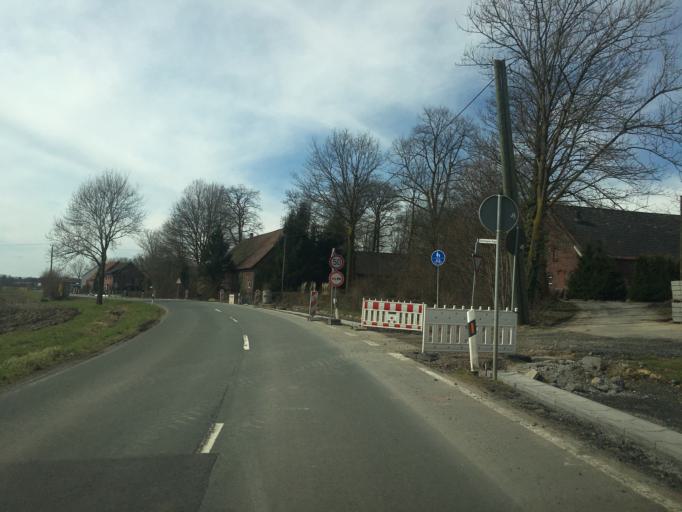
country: DE
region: North Rhine-Westphalia
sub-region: Regierungsbezirk Munster
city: Nordkirchen
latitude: 51.7299
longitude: 7.5784
